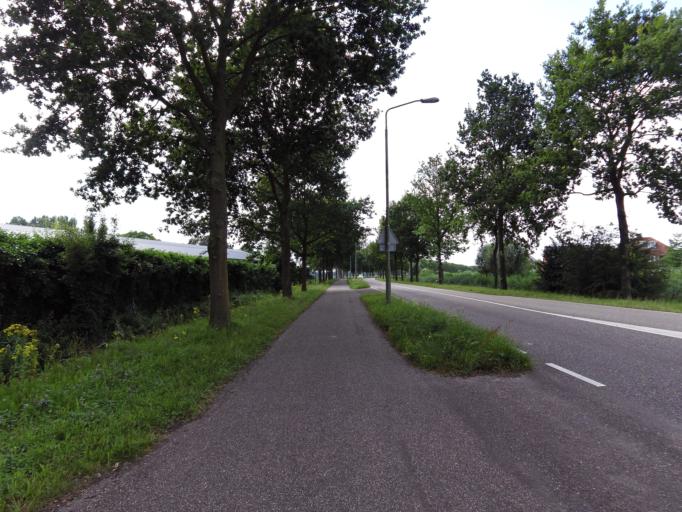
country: NL
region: South Holland
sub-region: Gemeente Sliedrecht
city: Sliedrecht
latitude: 51.7900
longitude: 4.7317
